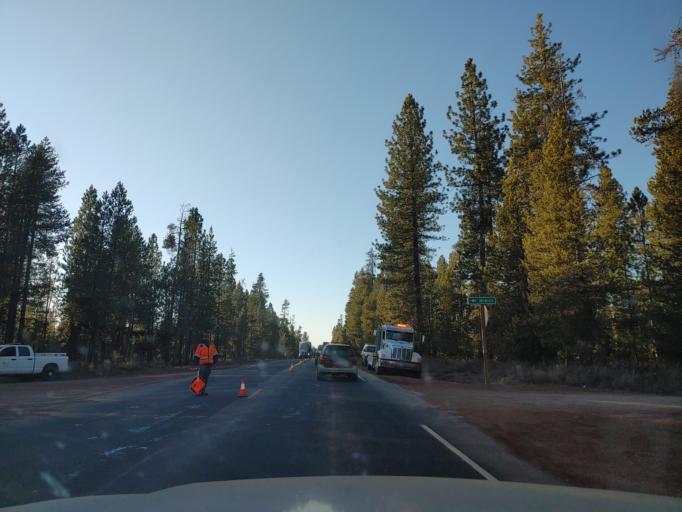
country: US
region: Oregon
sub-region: Deschutes County
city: La Pine
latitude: 43.3824
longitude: -121.8031
